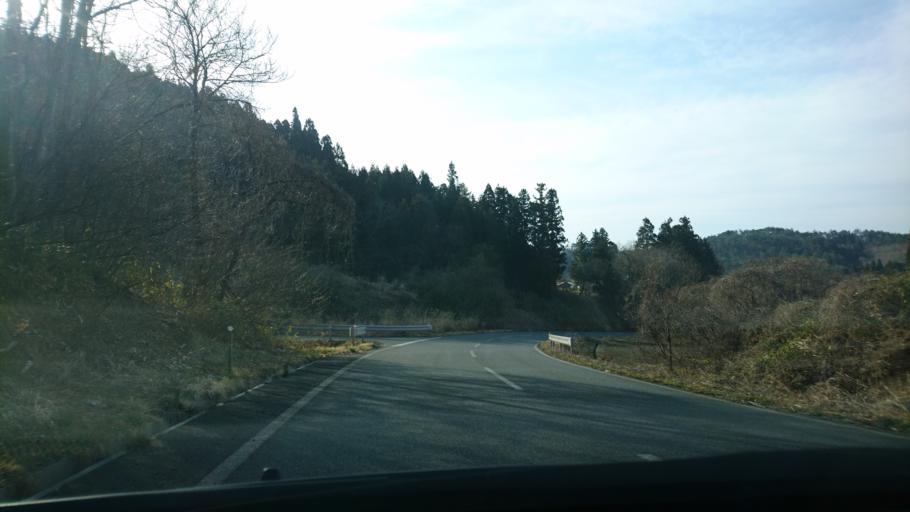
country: JP
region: Iwate
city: Ichinoseki
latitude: 38.8364
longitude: 141.2187
